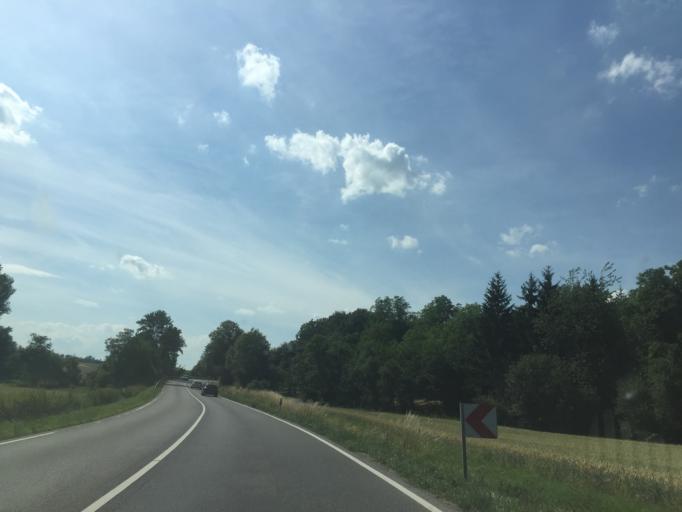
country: DE
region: Baden-Wuerttemberg
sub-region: Karlsruhe Region
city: Sinsheim
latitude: 49.2648
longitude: 8.8472
